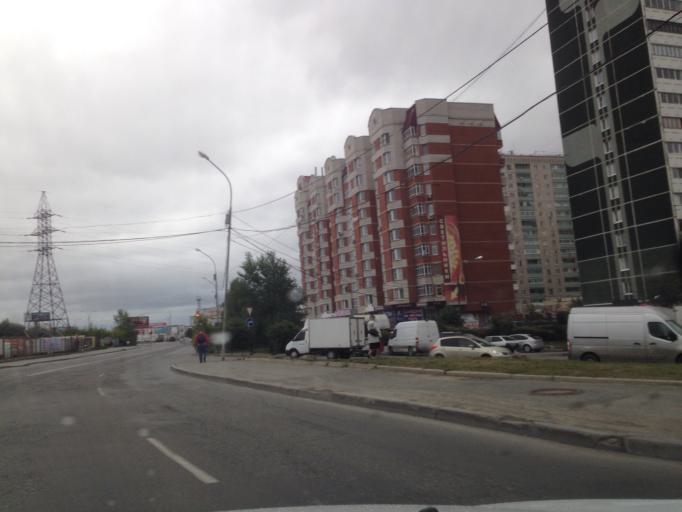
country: RU
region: Sverdlovsk
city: Yekaterinburg
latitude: 56.8432
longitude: 60.6879
